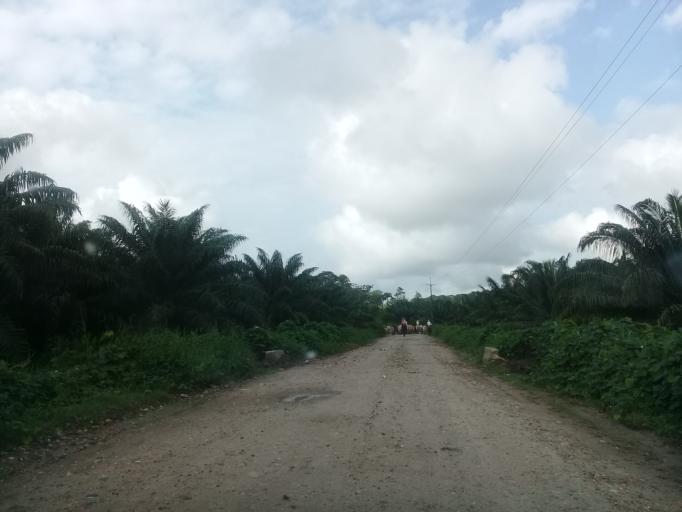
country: CO
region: Antioquia
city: Puerto Triunfo
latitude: 5.7087
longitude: -74.5566
